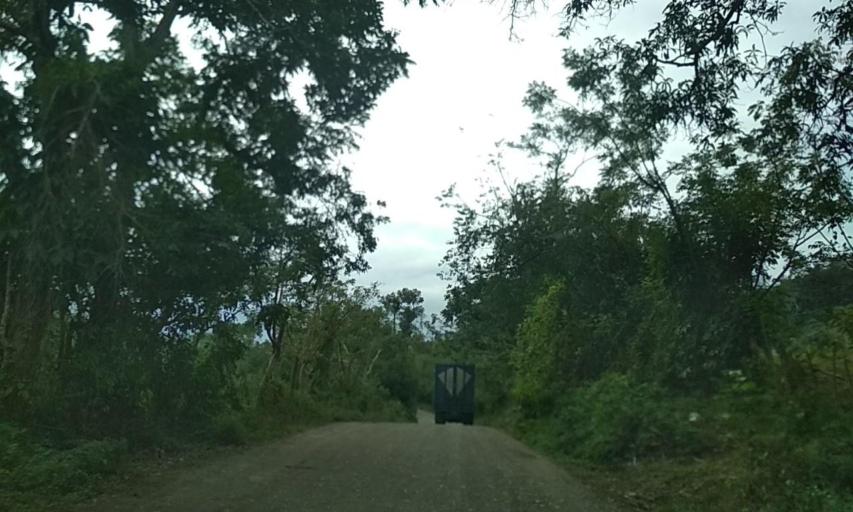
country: MX
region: Veracruz
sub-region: Papantla
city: Residencial Tajin
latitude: 20.6281
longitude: -97.3637
